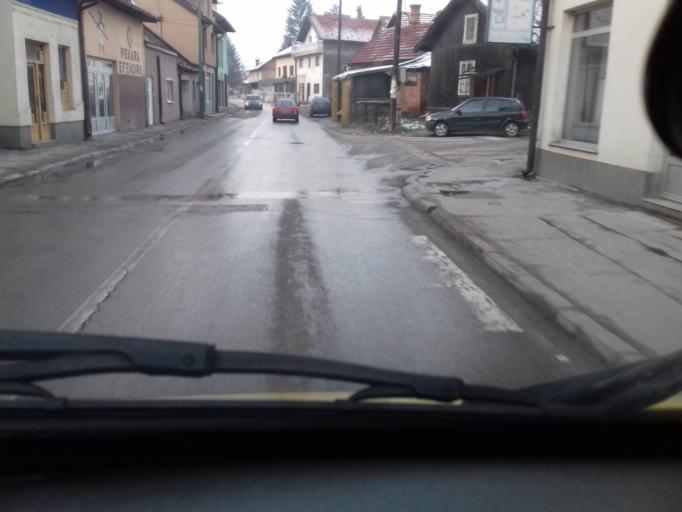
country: BA
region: Federation of Bosnia and Herzegovina
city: Visoko
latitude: 43.9932
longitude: 18.1845
